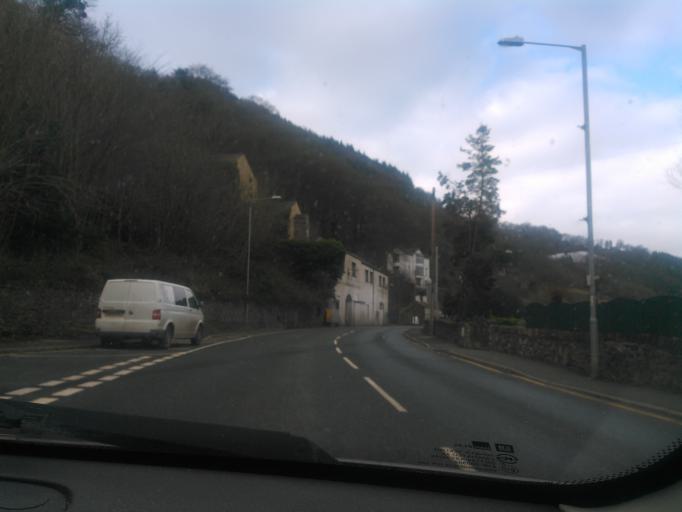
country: GB
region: Wales
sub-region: Denbighshire
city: Llangollen
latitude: 52.9695
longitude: -3.1752
